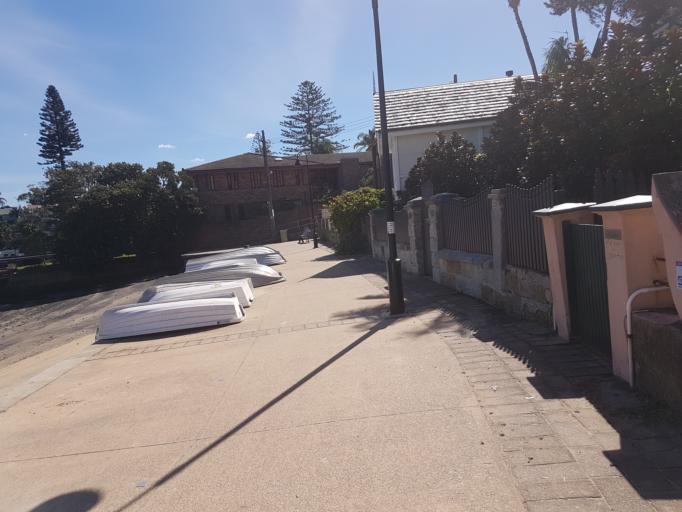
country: AU
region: New South Wales
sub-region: Waverley
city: Dover Heights
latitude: -33.8419
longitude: 151.2812
